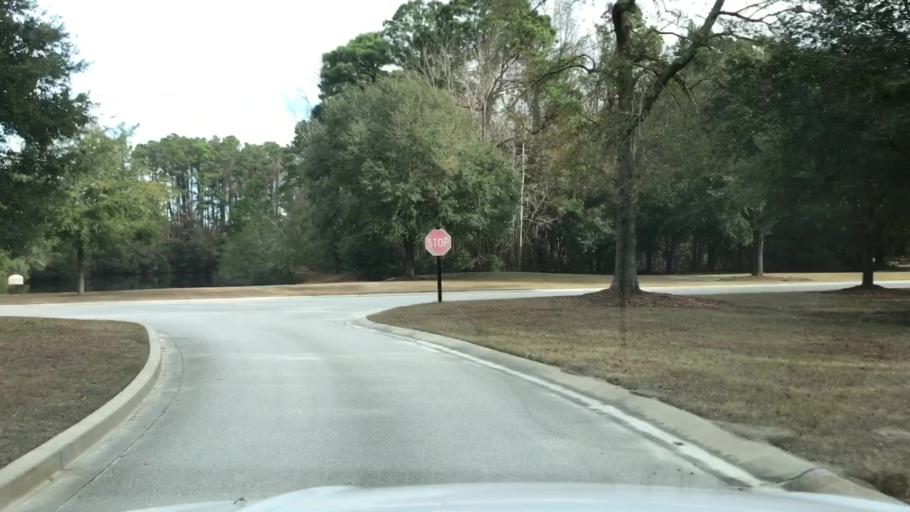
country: US
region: South Carolina
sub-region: Charleston County
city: Isle of Palms
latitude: 32.9060
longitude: -79.7199
